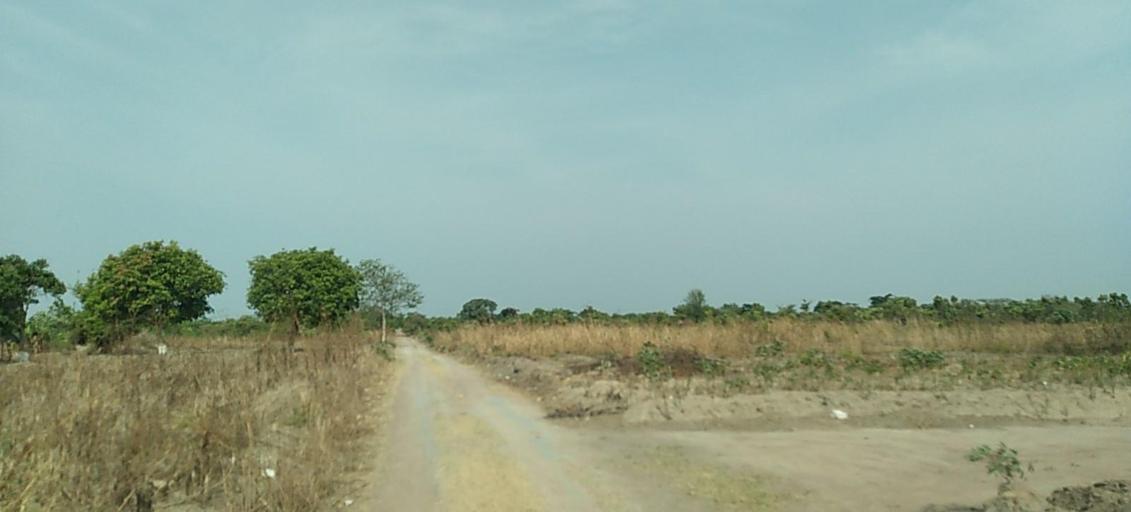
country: ZM
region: Copperbelt
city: Luanshya
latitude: -13.2175
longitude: 28.6508
